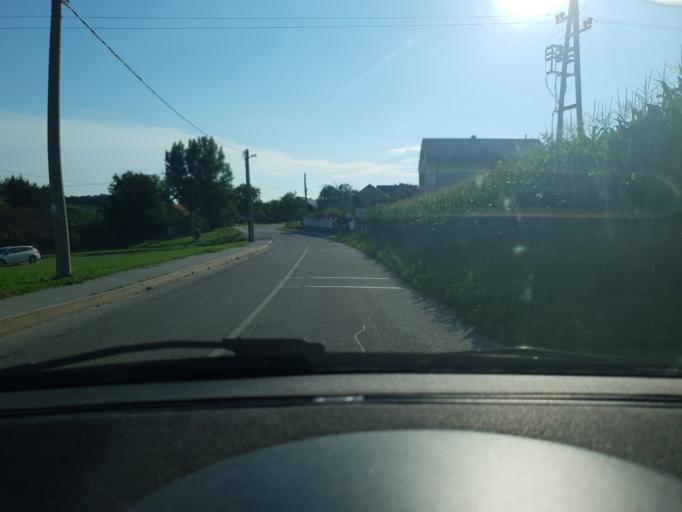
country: HR
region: Krapinsko-Zagorska
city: Radoboj
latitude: 46.1655
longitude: 15.9129
